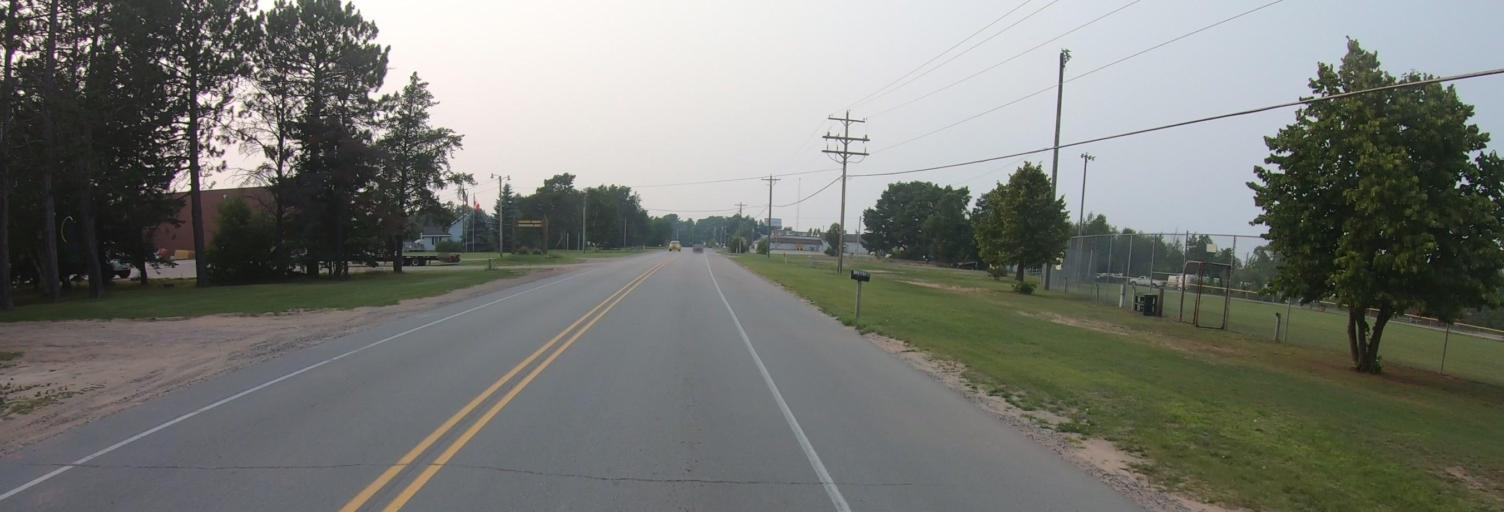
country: US
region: Michigan
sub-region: Chippewa County
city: Sault Ste. Marie
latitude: 46.4496
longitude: -84.5996
